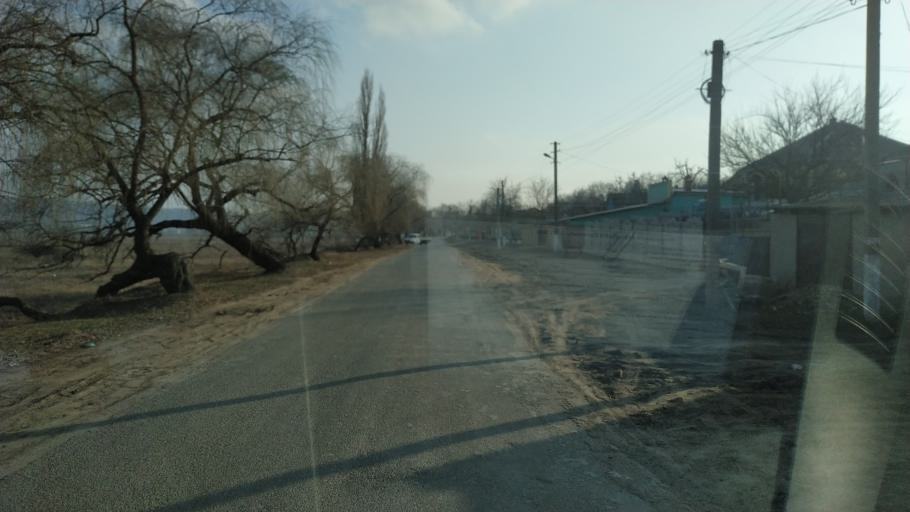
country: MD
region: Hincesti
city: Dancu
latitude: 46.7732
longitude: 28.3463
